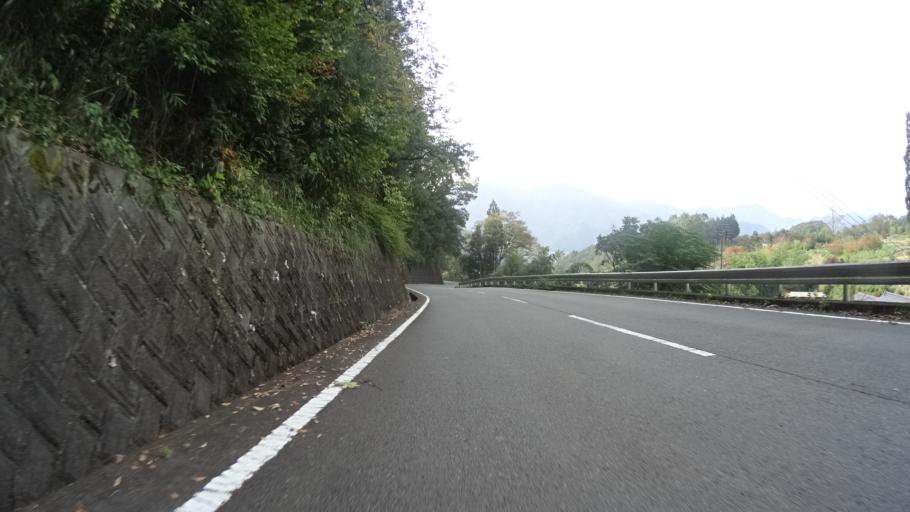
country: JP
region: Yamanashi
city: Otsuki
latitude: 35.6214
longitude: 139.0189
